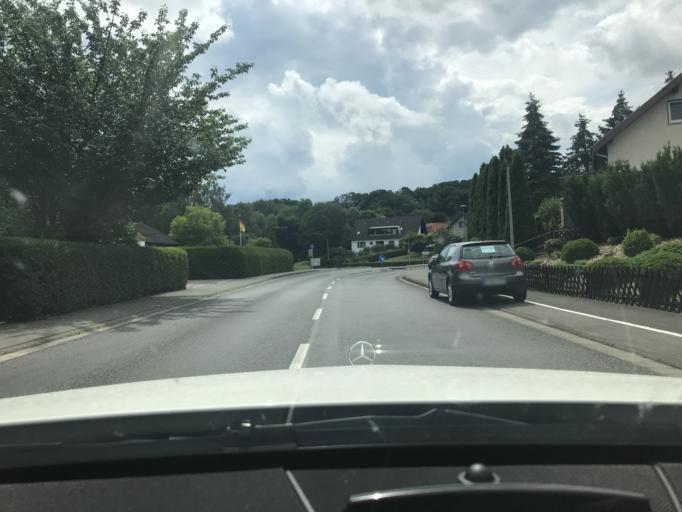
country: DE
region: Hesse
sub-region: Regierungsbezirk Kassel
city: Eschwege
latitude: 51.1817
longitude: 10.0710
